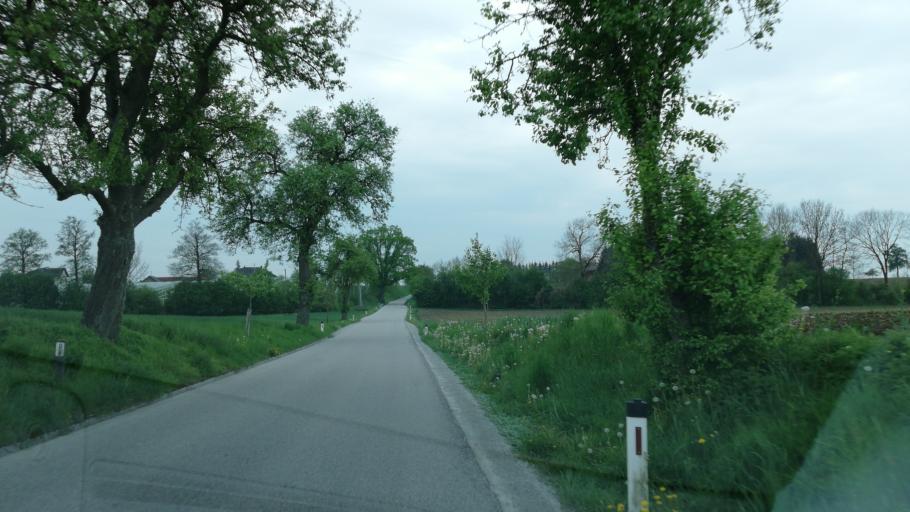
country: AT
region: Upper Austria
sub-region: Wels-Land
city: Buchkirchen
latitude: 48.2316
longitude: 14.0579
